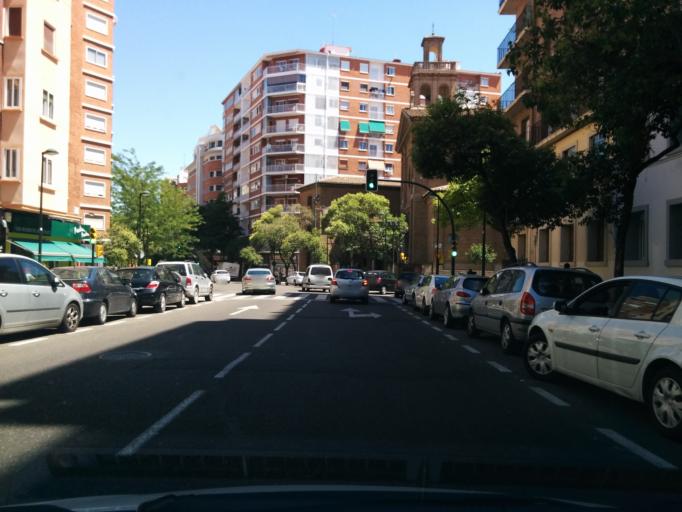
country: ES
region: Aragon
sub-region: Provincia de Zaragoza
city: Delicias
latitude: 41.6414
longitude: -0.8930
